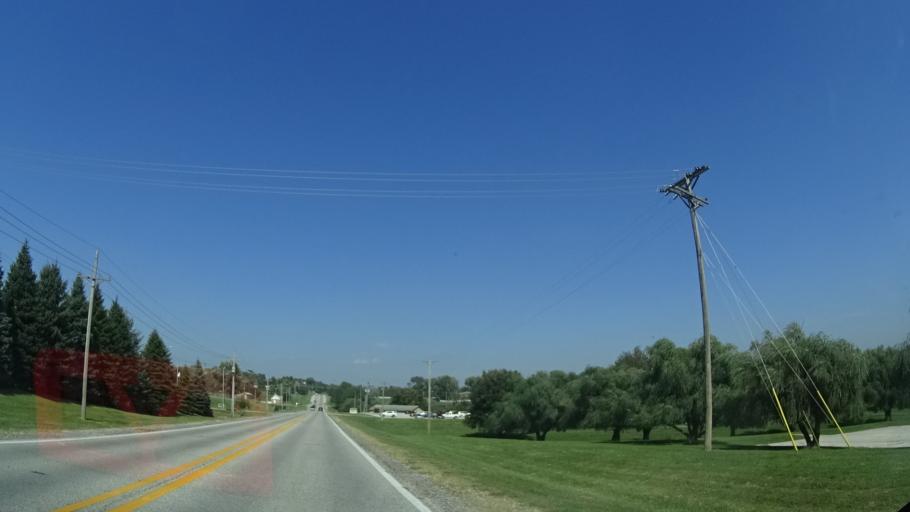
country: US
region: Nebraska
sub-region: Sarpy County
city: Offutt Air Force Base
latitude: 41.1257
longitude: -95.9474
